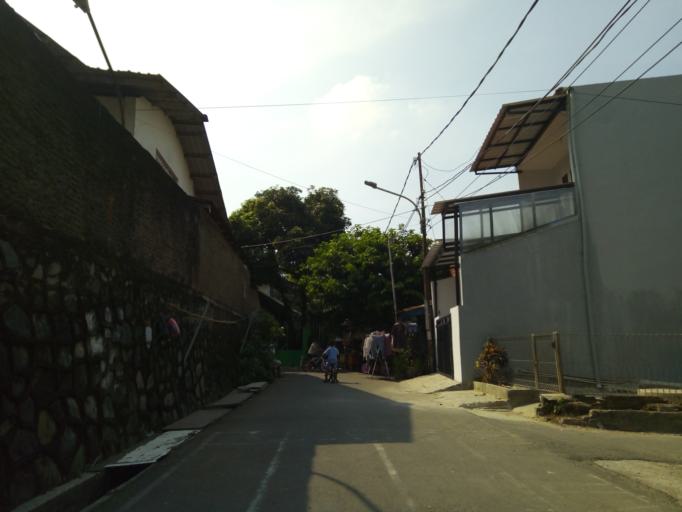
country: ID
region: Jakarta Raya
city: Jakarta
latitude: -6.2053
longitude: 106.8303
